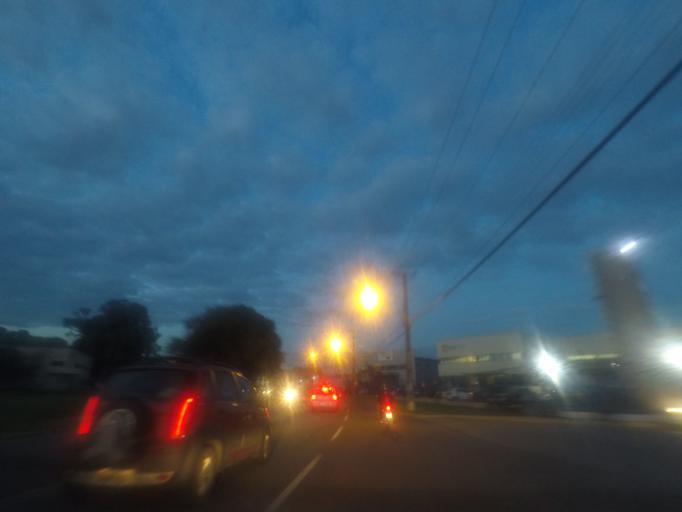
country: BR
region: Parana
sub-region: Pinhais
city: Pinhais
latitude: -25.3930
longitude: -49.1885
